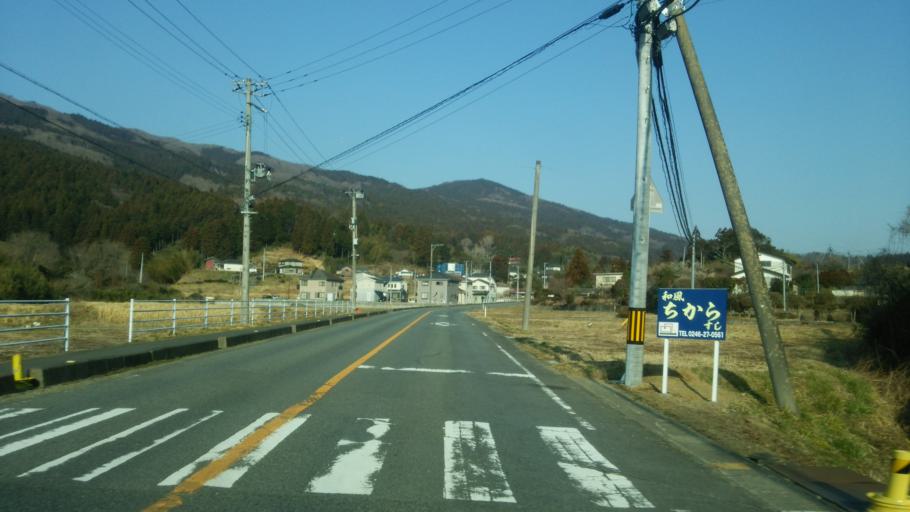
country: JP
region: Fukushima
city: Iwaki
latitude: 37.0461
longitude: 140.7996
